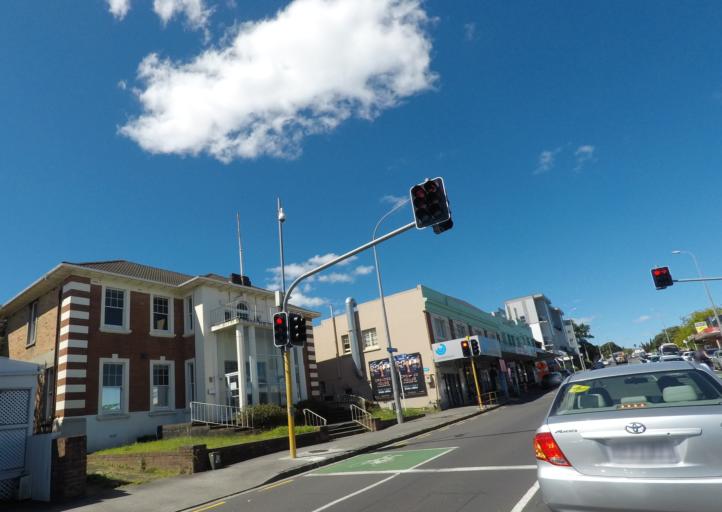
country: NZ
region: Auckland
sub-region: Auckland
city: Auckland
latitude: -36.8738
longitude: 174.7363
